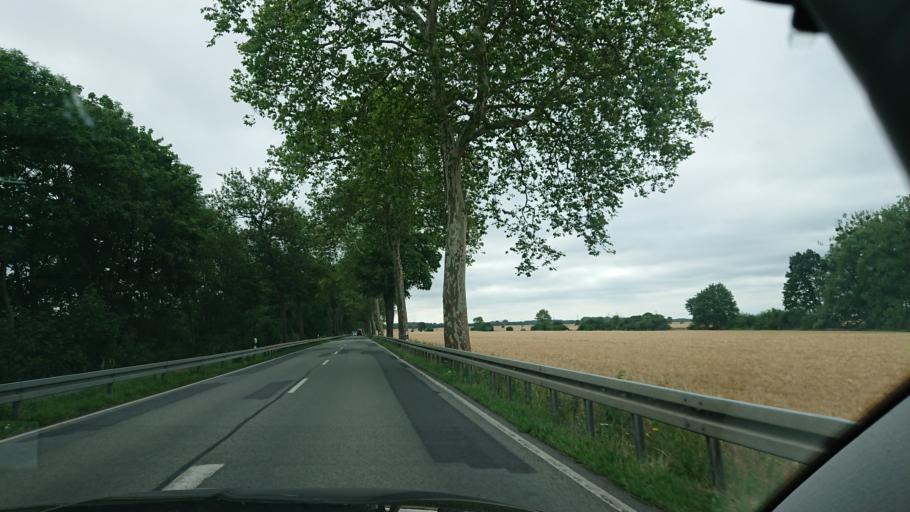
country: DE
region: Brandenburg
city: Perleberg
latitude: 53.0457
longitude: 11.9366
